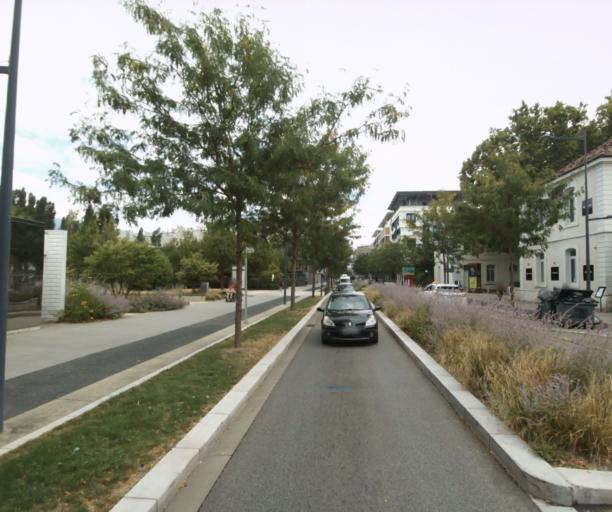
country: FR
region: Rhone-Alpes
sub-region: Departement de l'Isere
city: Grenoble
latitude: 45.1844
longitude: 5.7259
